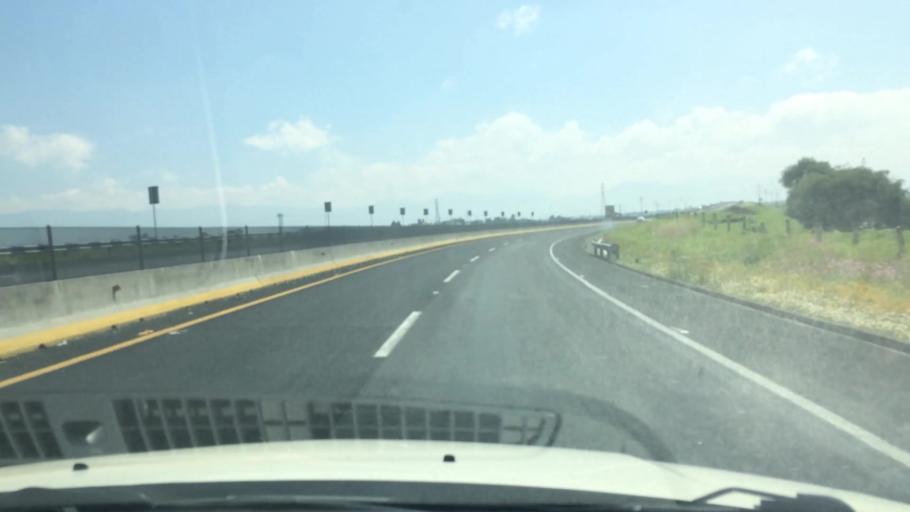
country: MX
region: Mexico
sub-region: Otzolotepec
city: La Y
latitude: 19.4066
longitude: -99.5992
